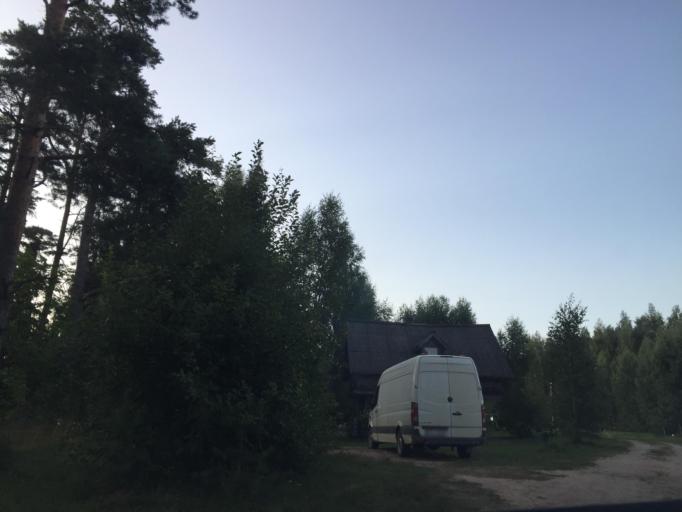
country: LV
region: Talsu Rajons
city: Stende
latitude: 57.1623
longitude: 22.3041
